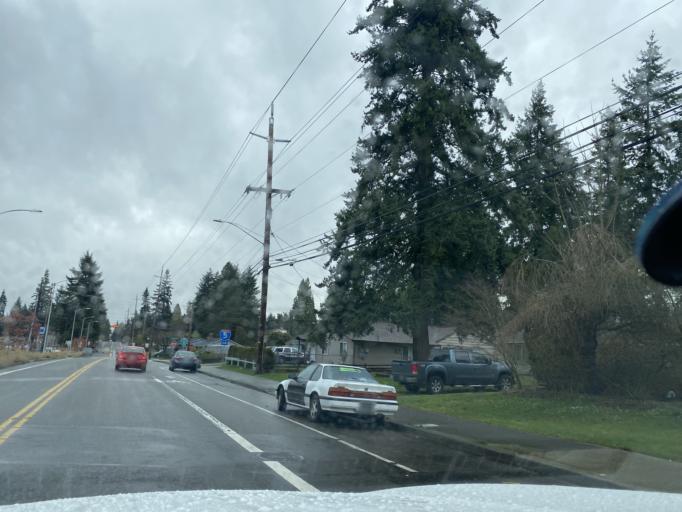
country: US
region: Washington
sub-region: Snohomish County
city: Mountlake Terrace
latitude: 47.8002
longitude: -122.3031
